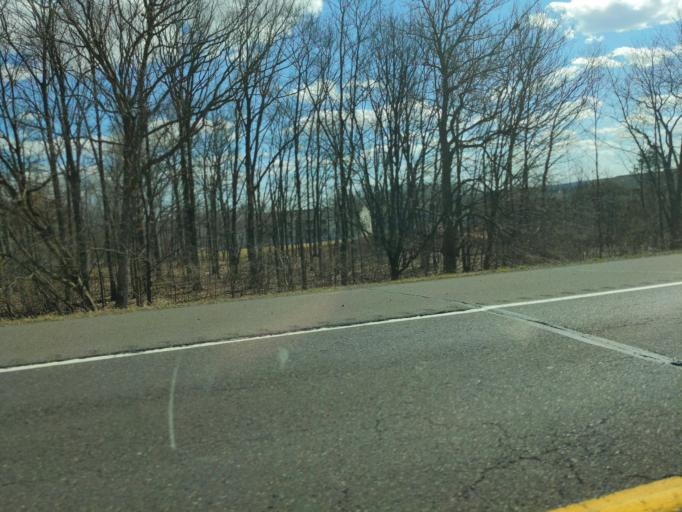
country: US
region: Pennsylvania
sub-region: Montgomery County
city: Pennsburg
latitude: 40.4080
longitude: -75.4816
